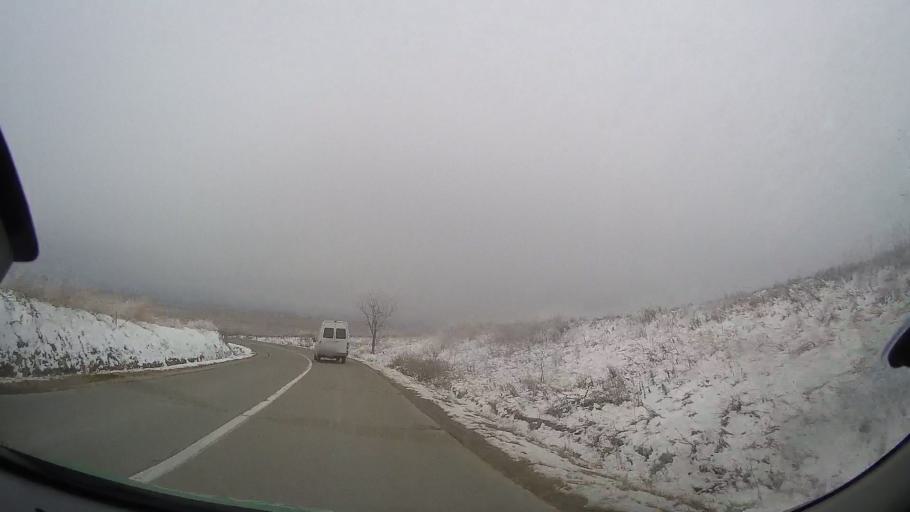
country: RO
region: Vaslui
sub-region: Comuna Grivita
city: Grivita
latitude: 46.1943
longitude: 27.6031
